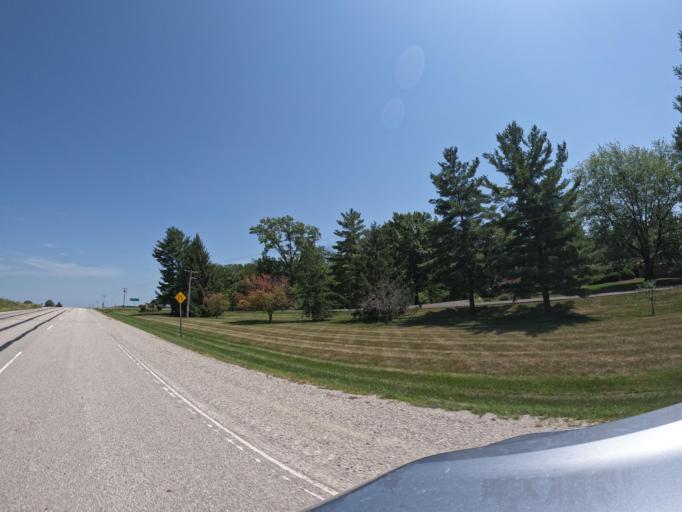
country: US
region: Iowa
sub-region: Henry County
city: Mount Pleasant
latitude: 40.9671
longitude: -91.6235
